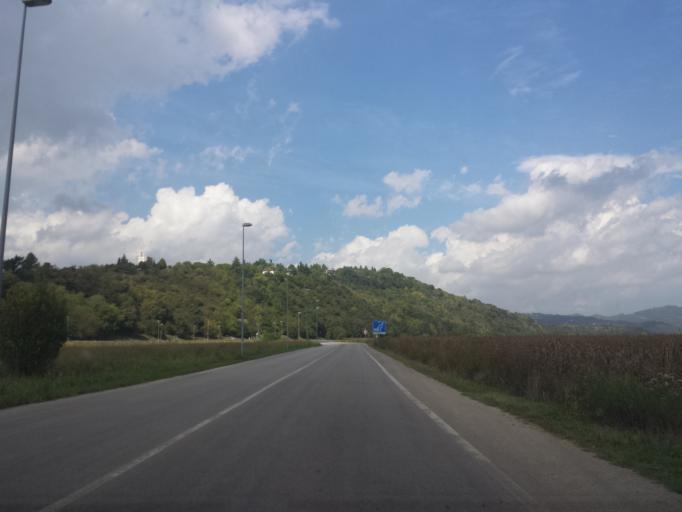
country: IT
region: Veneto
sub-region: Provincia di Vicenza
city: Sovizzo
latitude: 45.5323
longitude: 11.4471
